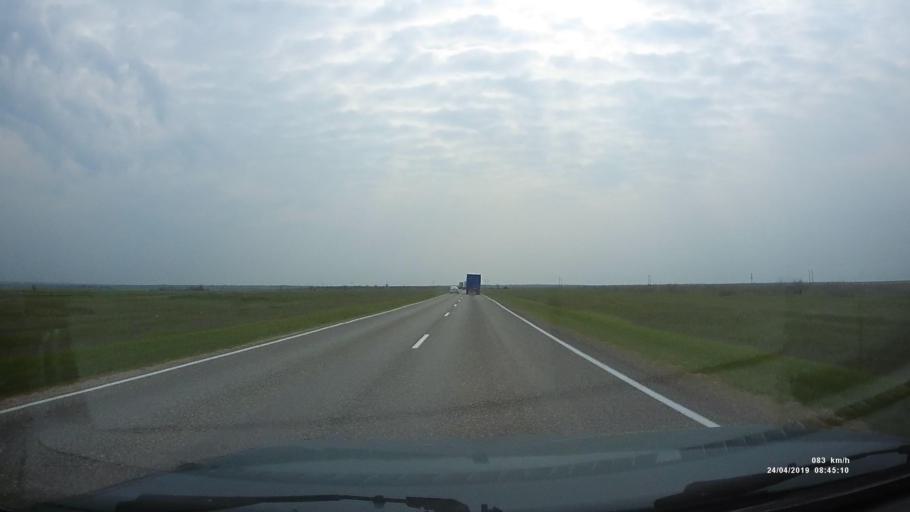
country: RU
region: Kalmykiya
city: Arshan'
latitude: 46.2368
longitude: 44.0559
